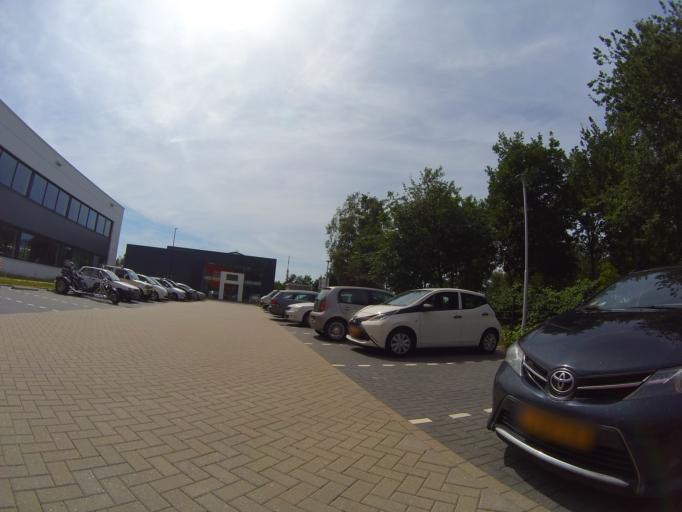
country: NL
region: Utrecht
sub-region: Gemeente Soest
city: Soest
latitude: 52.1185
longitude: 5.3050
